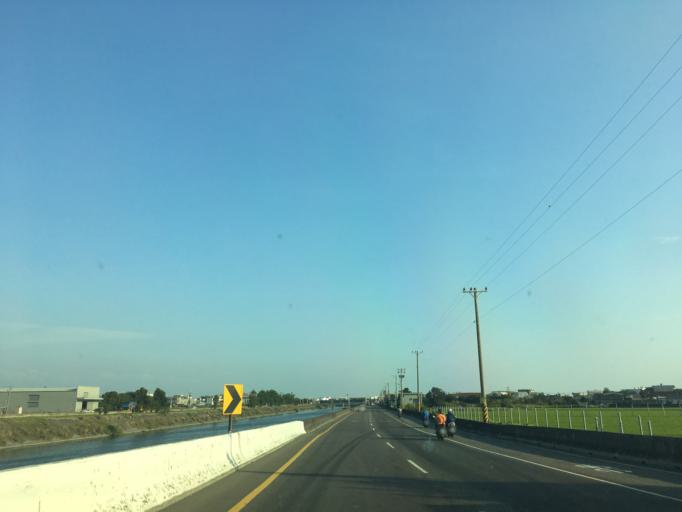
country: TW
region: Taiwan
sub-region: Changhua
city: Chang-hua
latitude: 24.0346
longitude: 120.4433
